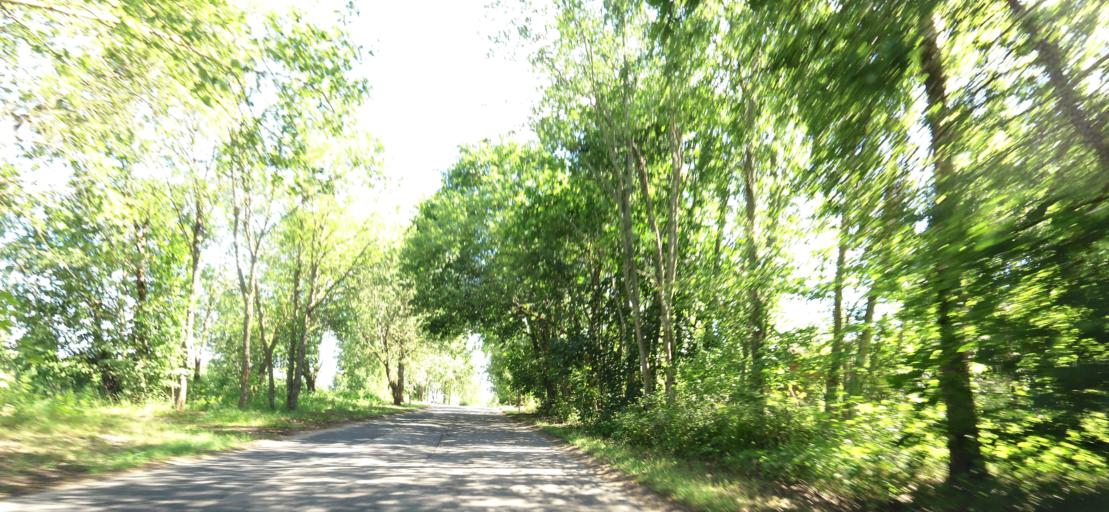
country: LT
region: Vilnius County
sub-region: Vilnius
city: Fabijoniskes
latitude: 54.8122
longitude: 25.3230
